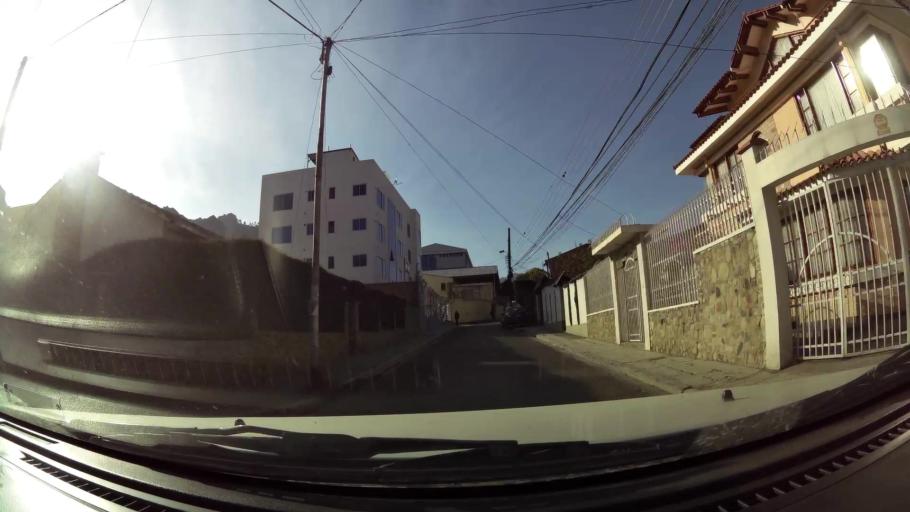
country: BO
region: La Paz
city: La Paz
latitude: -16.5227
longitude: -68.0898
